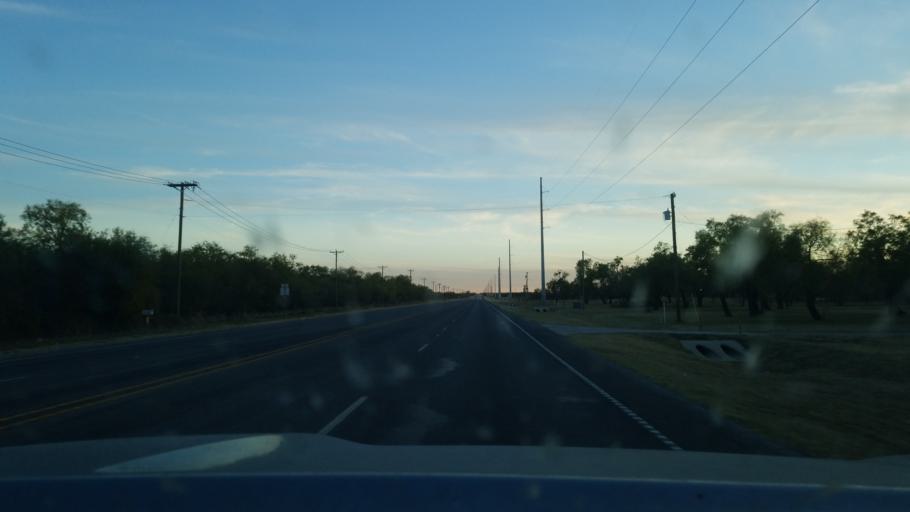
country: US
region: Texas
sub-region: Stephens County
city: Breckenridge
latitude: 32.7358
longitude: -98.9026
